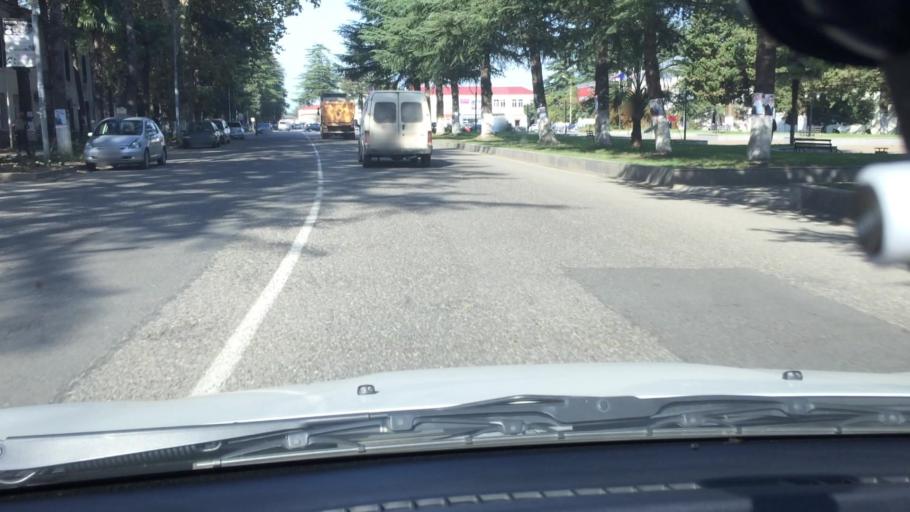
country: GE
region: Guria
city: Lanchkhuti
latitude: 42.0867
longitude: 42.0379
